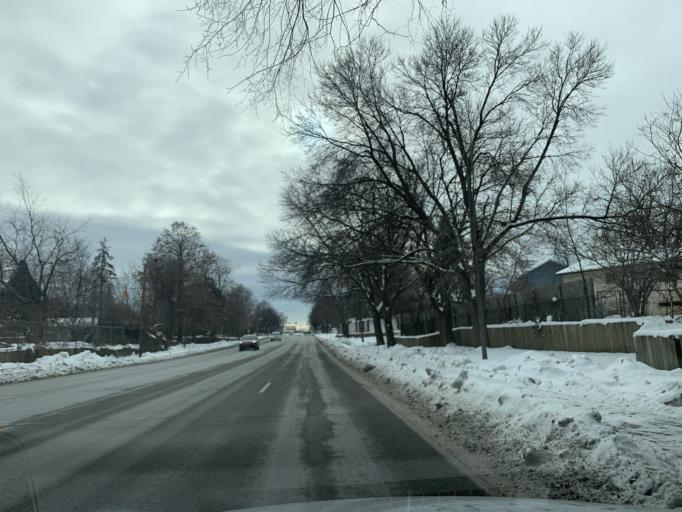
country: US
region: Minnesota
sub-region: Hennepin County
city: Minneapolis
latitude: 44.9946
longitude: -93.2881
